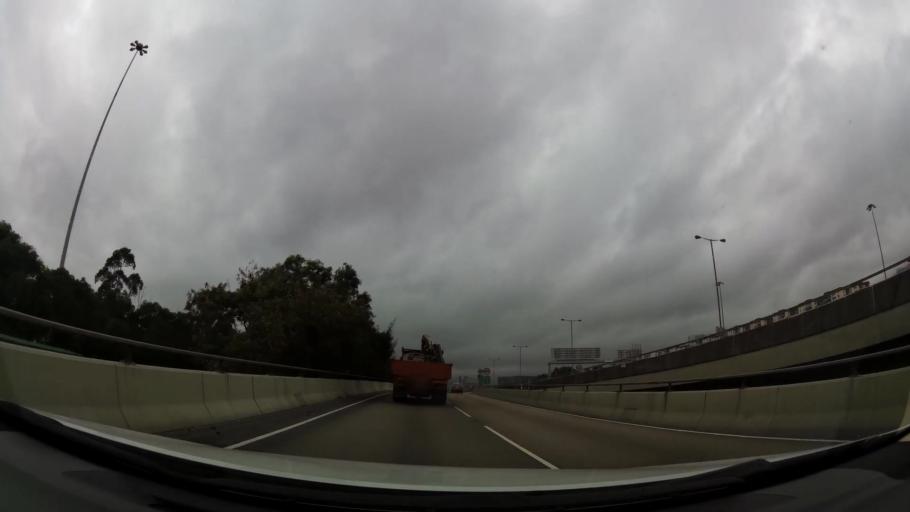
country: HK
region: Sham Shui Po
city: Sham Shui Po
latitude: 22.3321
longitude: 114.1409
